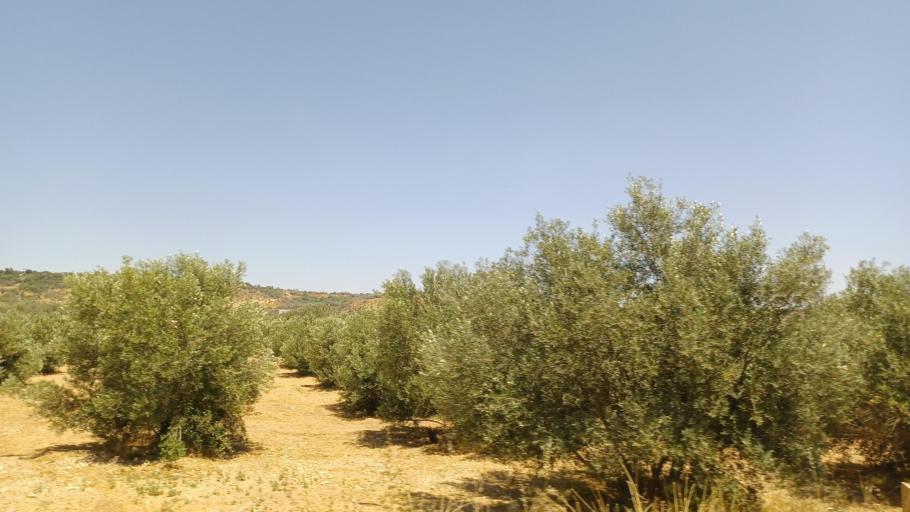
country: CY
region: Larnaka
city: Pyla
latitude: 35.0060
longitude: 33.7003
